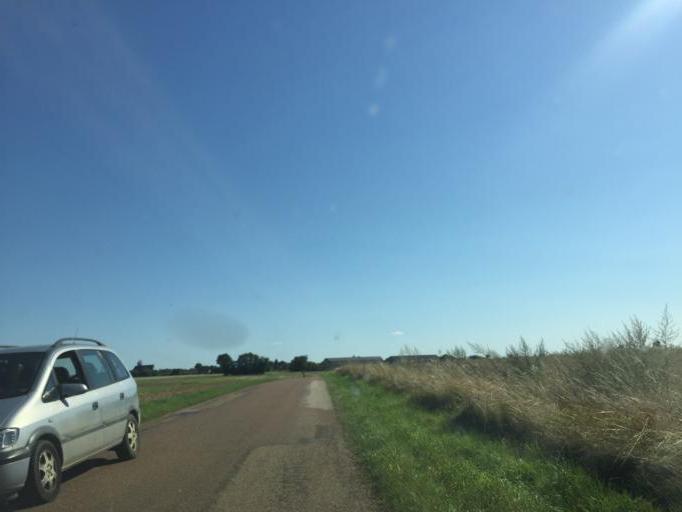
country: FR
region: Bourgogne
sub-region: Departement de l'Yonne
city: Fontenailles
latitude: 47.5145
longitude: 3.3454
